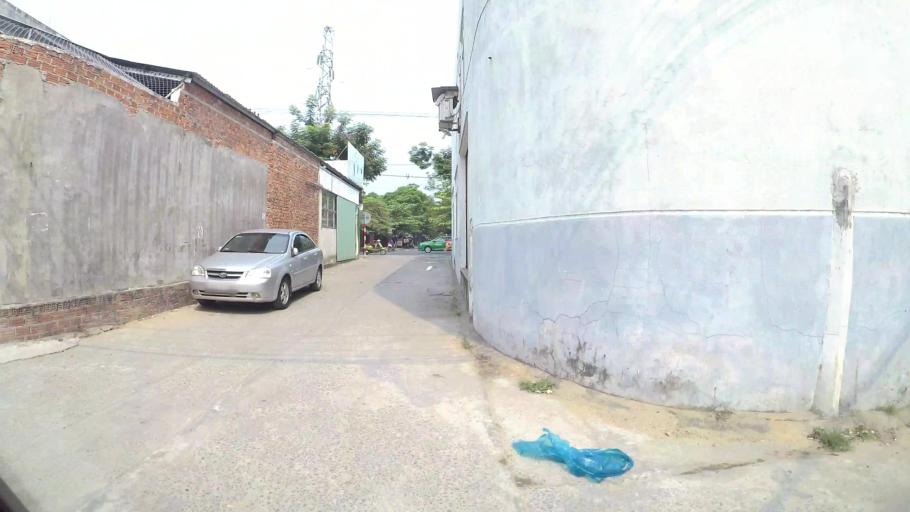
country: VN
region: Da Nang
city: Son Tra
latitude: 16.0433
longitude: 108.2172
